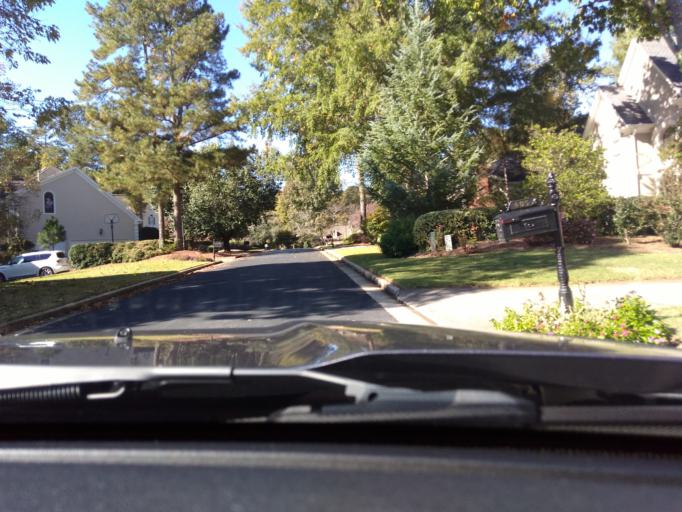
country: US
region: Georgia
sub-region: Fulton County
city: Johns Creek
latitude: 34.0206
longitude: -84.1850
